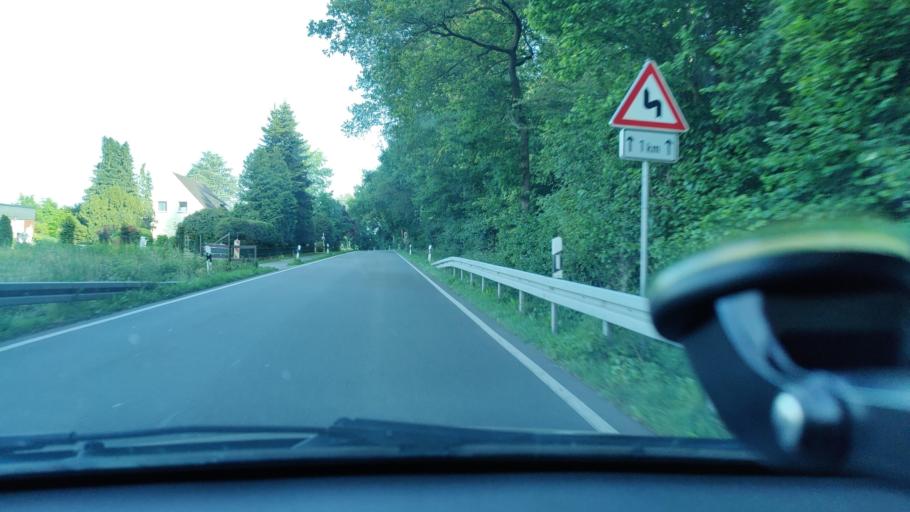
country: DE
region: North Rhine-Westphalia
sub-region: Regierungsbezirk Munster
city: Billerbeck
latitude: 51.9991
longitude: 7.2282
